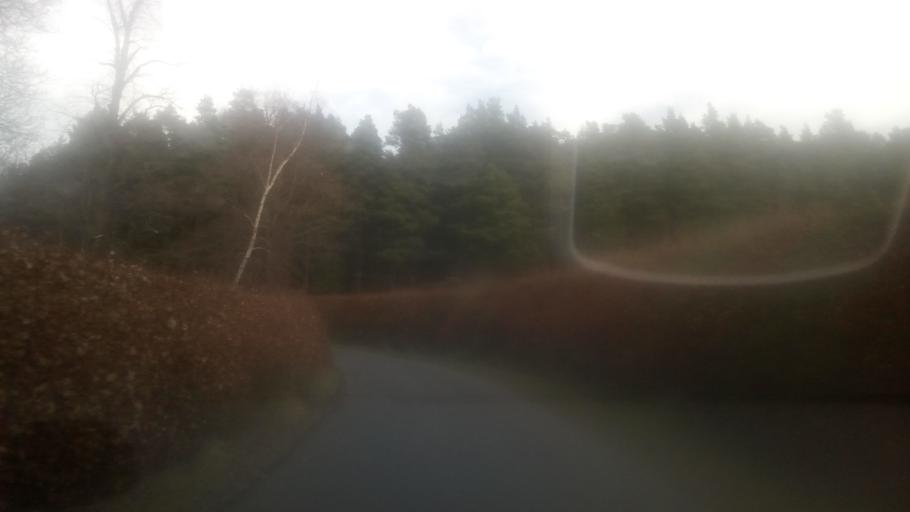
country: GB
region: Scotland
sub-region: The Scottish Borders
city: Jedburgh
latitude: 55.4787
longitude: -2.5265
